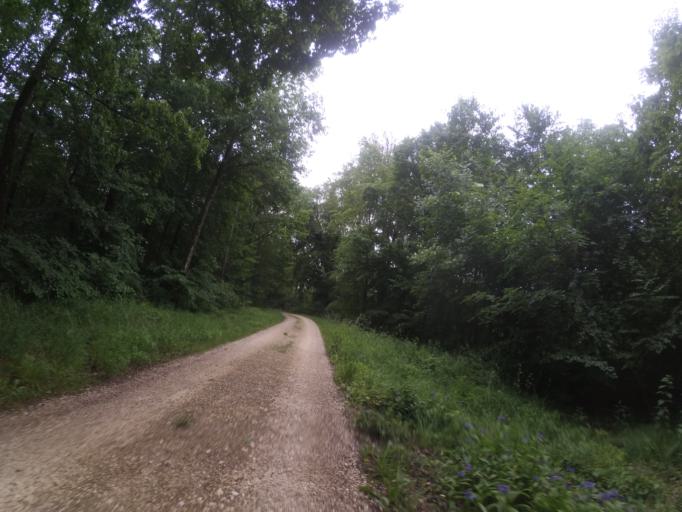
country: DE
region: Baden-Wuerttemberg
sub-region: Tuebingen Region
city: Borslingen
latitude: 48.5099
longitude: 10.0705
